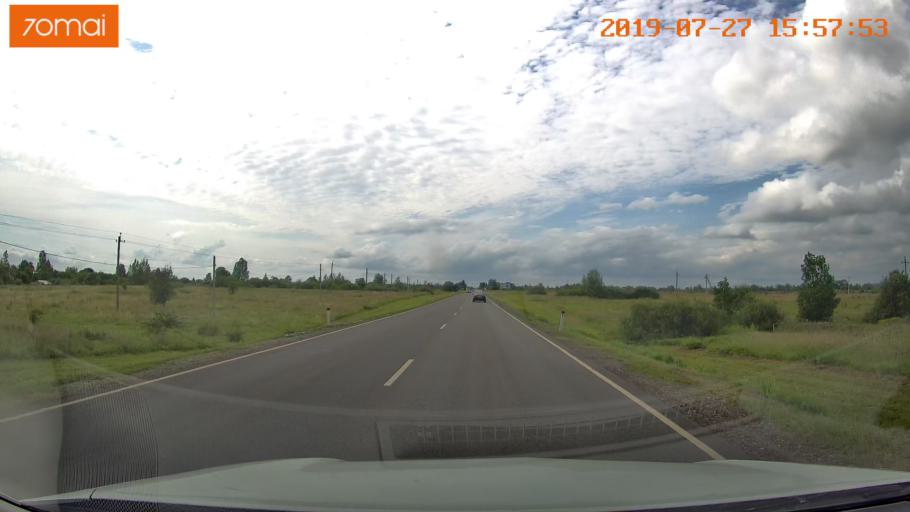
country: RU
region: Kaliningrad
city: Chernyakhovsk
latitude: 54.6252
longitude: 21.8751
